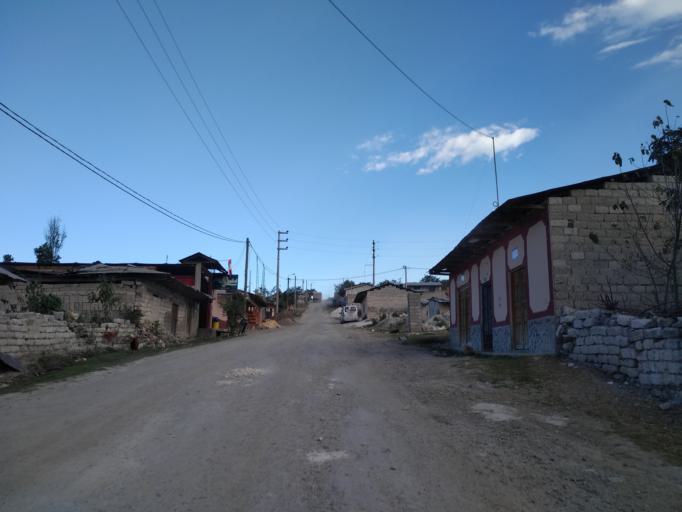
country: PE
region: Amazonas
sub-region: Provincia de Luya
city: Tingo
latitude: -6.3739
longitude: -77.9115
